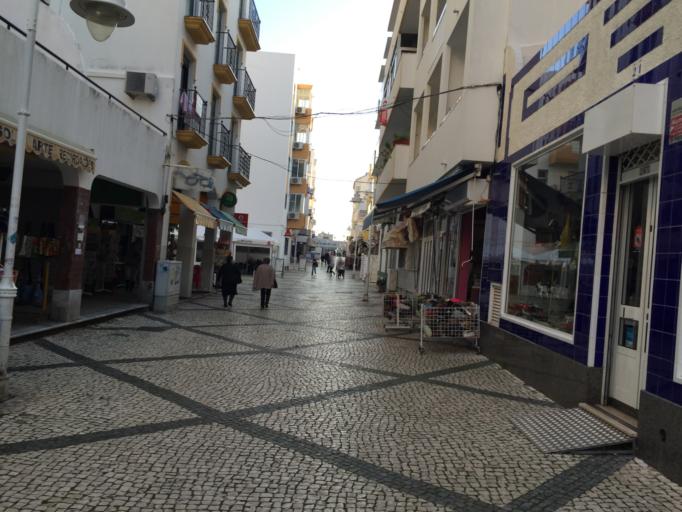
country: PT
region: Faro
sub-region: Vila Real de Santo Antonio
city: Monte Gordo
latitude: 37.1812
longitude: -7.4517
